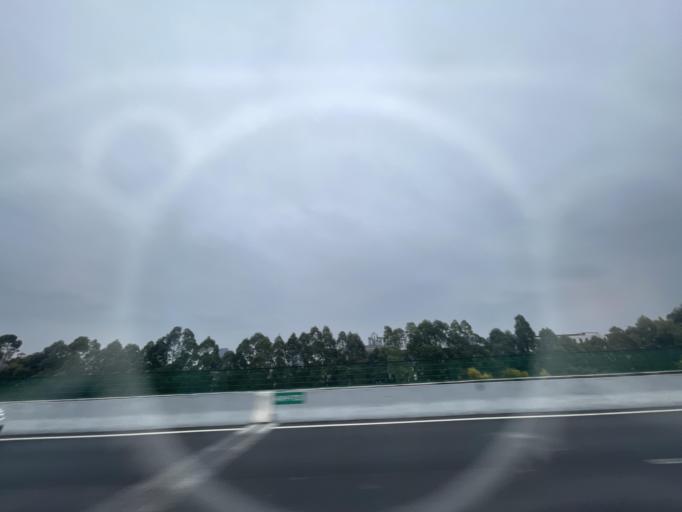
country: CN
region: Guangdong
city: Huangge
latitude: 22.7878
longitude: 113.5221
